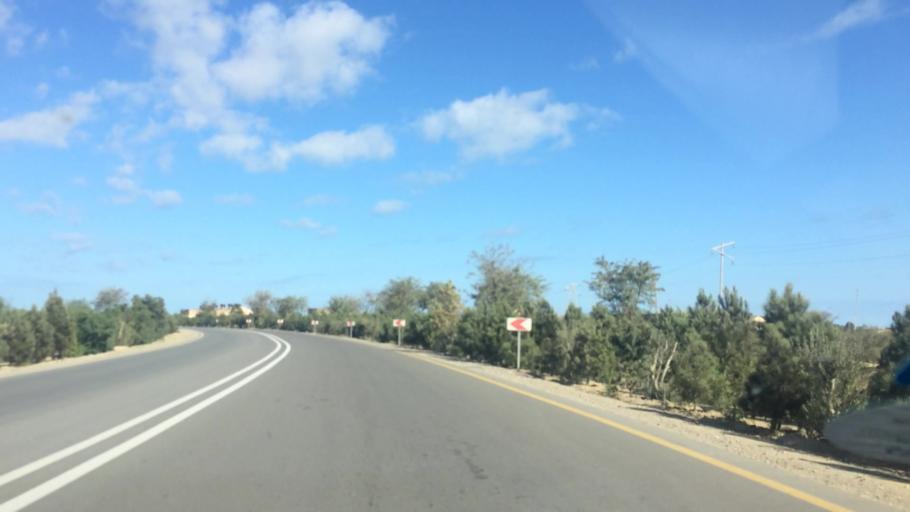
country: AZ
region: Baki
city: Pirallahi
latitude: 40.4226
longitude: 50.3565
